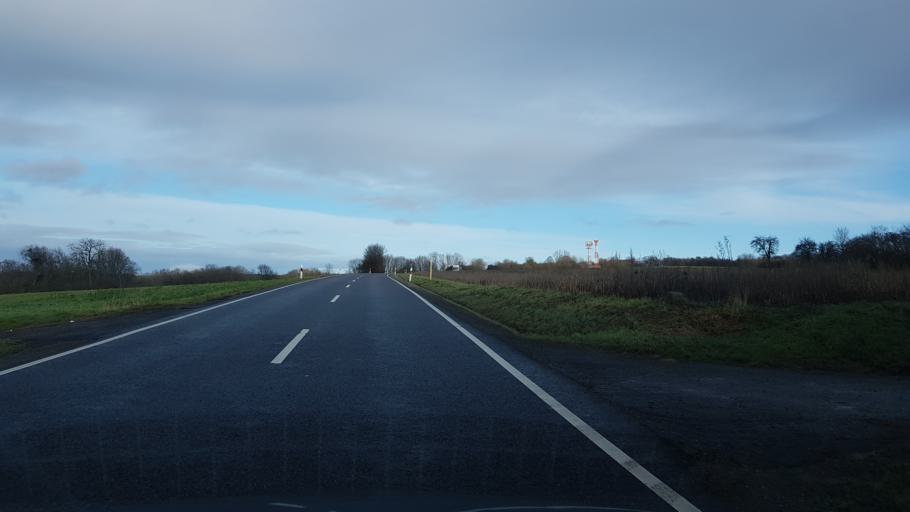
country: DE
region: Saarland
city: Sankt Ingbert
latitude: 49.2253
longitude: 7.1183
